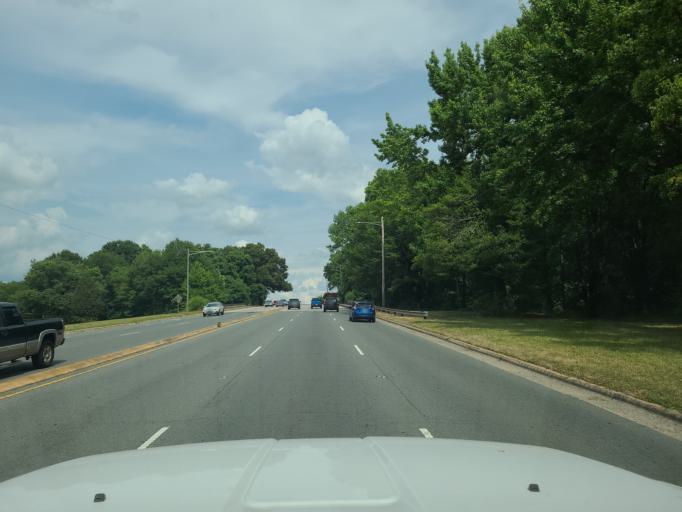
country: US
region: North Carolina
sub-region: Gaston County
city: Ranlo
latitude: 35.2617
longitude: -81.1487
